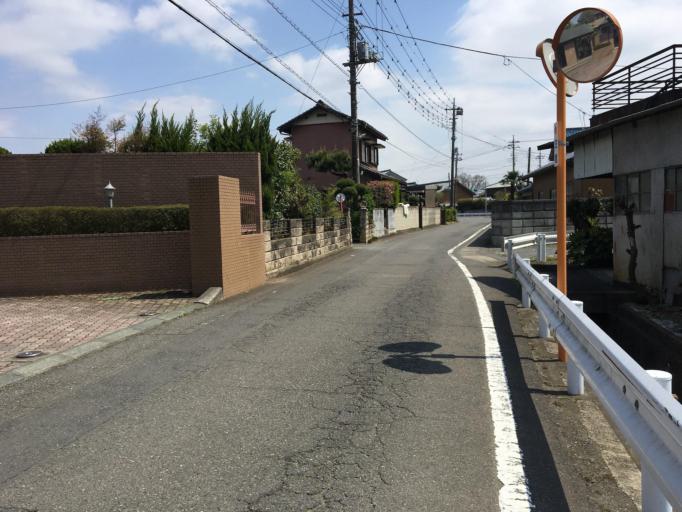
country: JP
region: Gunma
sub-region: Sawa-gun
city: Tamamura
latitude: 36.2879
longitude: 139.1582
